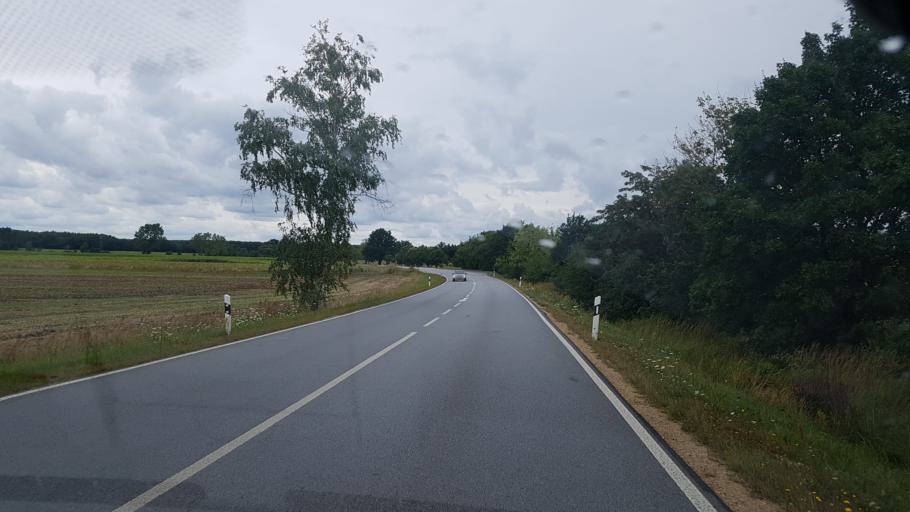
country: DE
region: Saxony
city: Niesky
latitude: 51.2572
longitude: 14.8090
